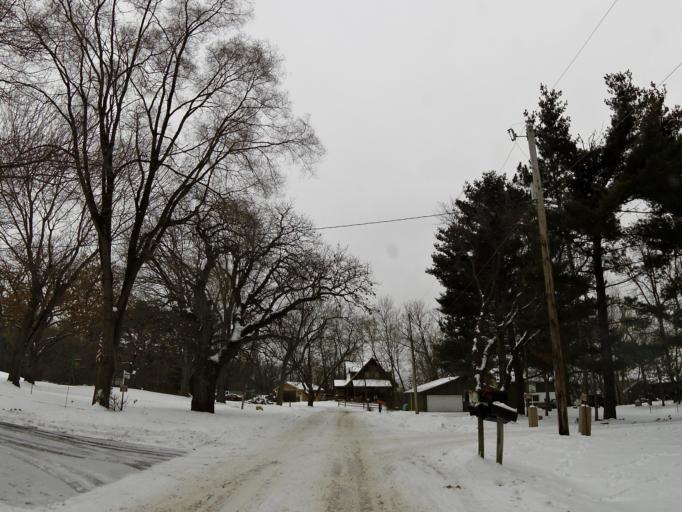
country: US
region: Minnesota
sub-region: Washington County
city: Stillwater
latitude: 45.0582
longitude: -92.7950
